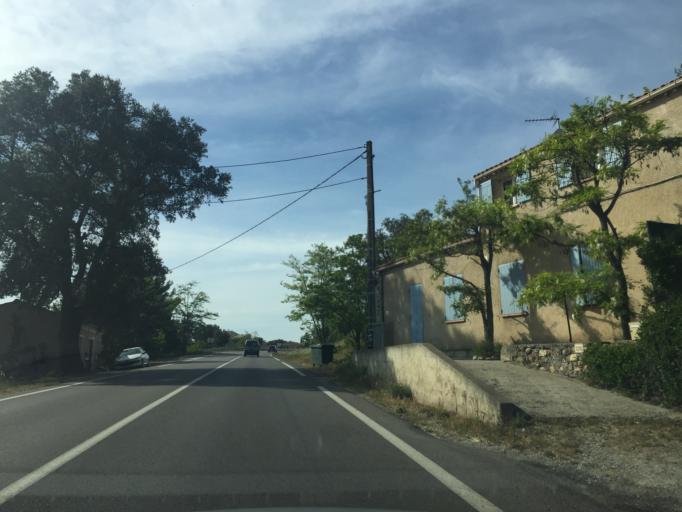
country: FR
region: Provence-Alpes-Cote d'Azur
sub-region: Departement du Var
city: Vinon-sur-Verdon
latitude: 43.7380
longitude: 5.8025
